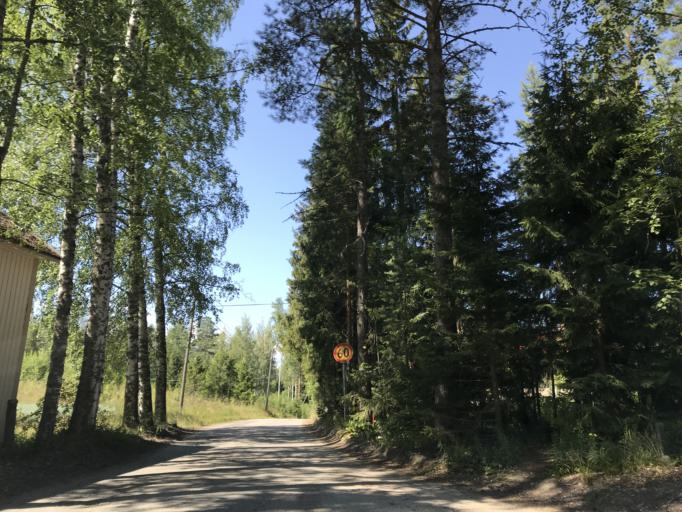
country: FI
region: Paijanne Tavastia
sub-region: Lahti
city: Asikkala
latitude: 61.1946
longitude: 25.6345
